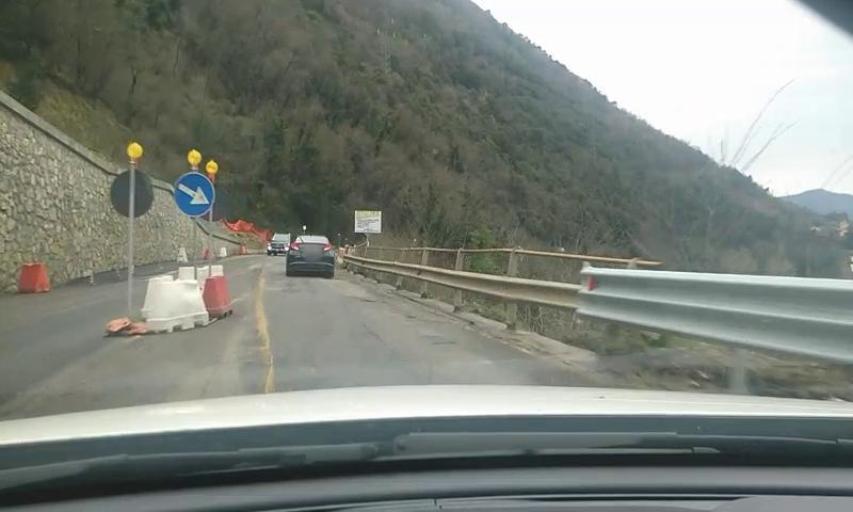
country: IT
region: Tuscany
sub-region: Provincia di Prato
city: Vaiano
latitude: 43.9270
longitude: 11.1270
